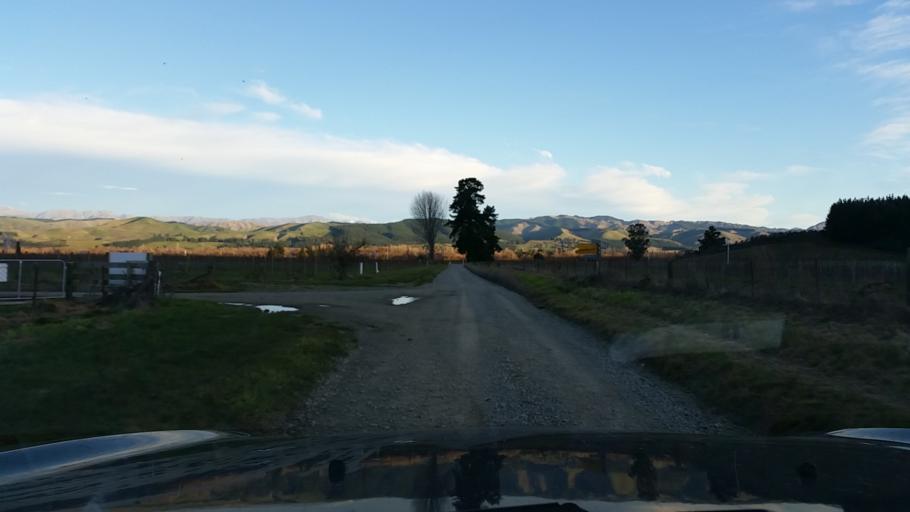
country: NZ
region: Marlborough
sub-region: Marlborough District
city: Blenheim
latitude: -41.5136
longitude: 173.5849
